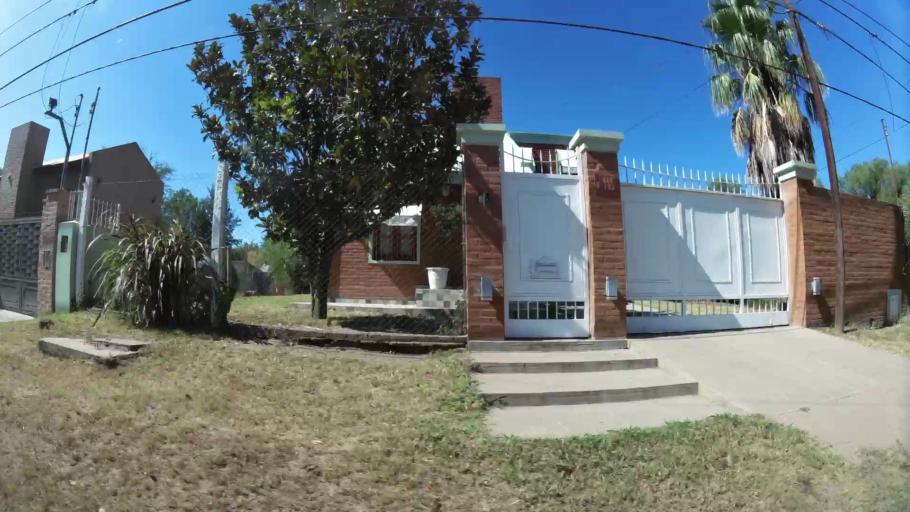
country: AR
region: Cordoba
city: Mendiolaza
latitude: -31.2708
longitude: -64.2977
